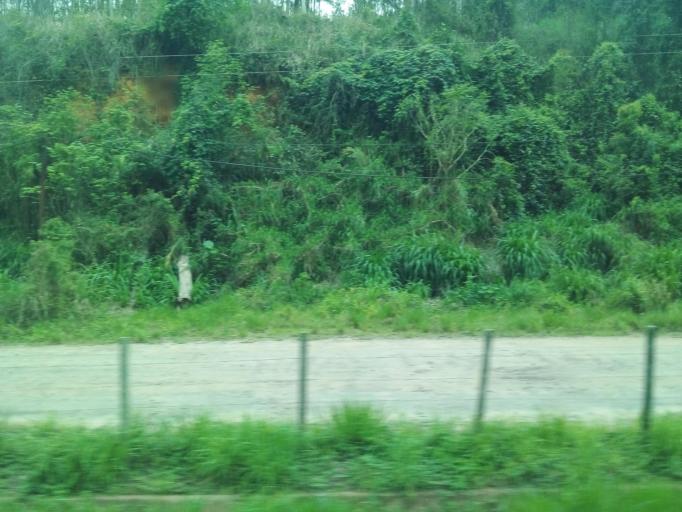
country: BR
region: Minas Gerais
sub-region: Nova Era
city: Nova Era
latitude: -19.7251
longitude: -42.9899
